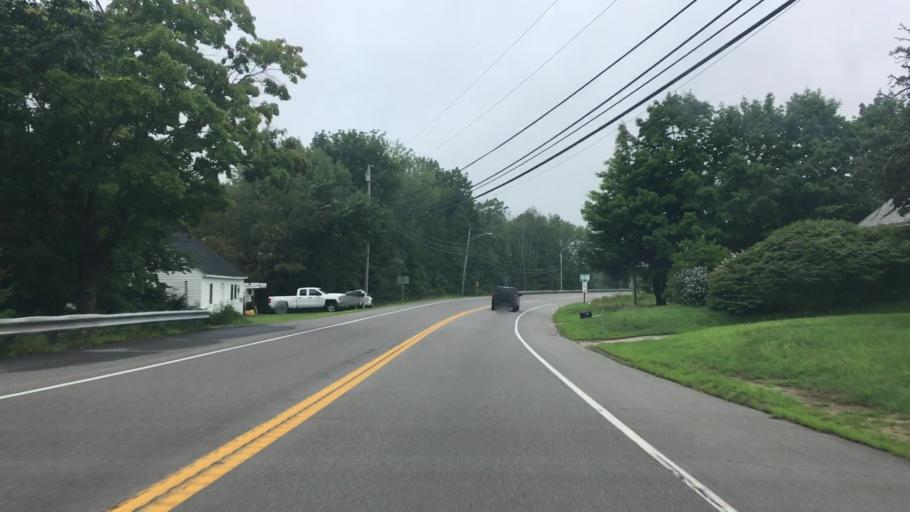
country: US
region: Maine
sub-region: York County
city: Lebanon
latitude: 43.4257
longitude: -70.8296
